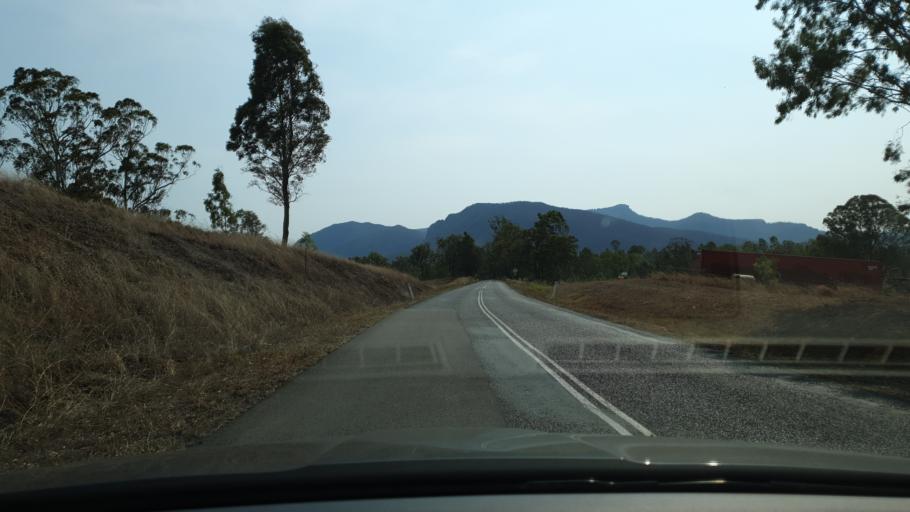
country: AU
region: Queensland
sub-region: Southern Downs
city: Warwick
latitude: -28.1740
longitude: 152.5468
